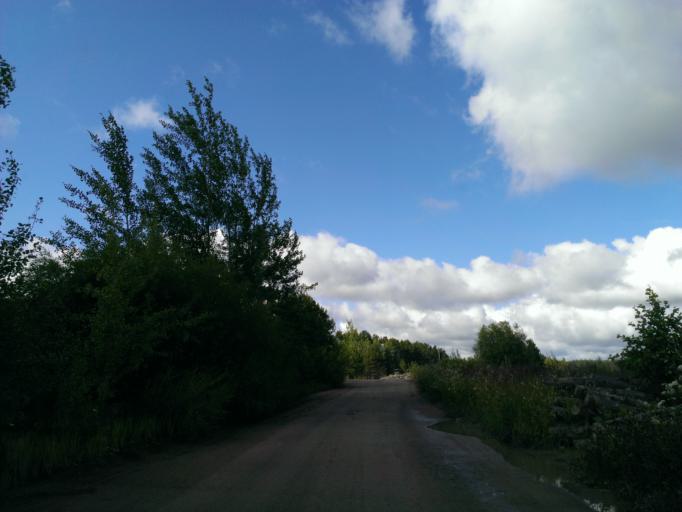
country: LV
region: Incukalns
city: Vangazi
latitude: 57.0887
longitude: 24.5132
